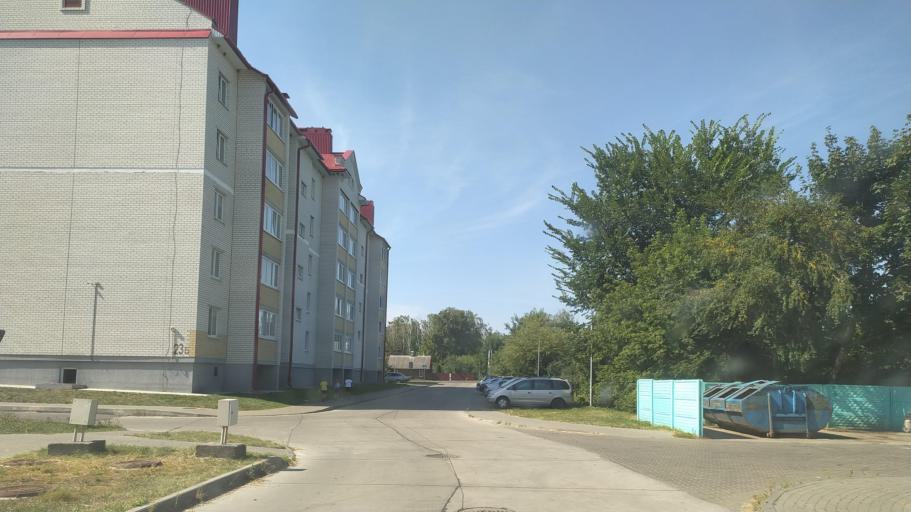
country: BY
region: Brest
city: Byaroza
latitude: 52.5373
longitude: 24.9938
